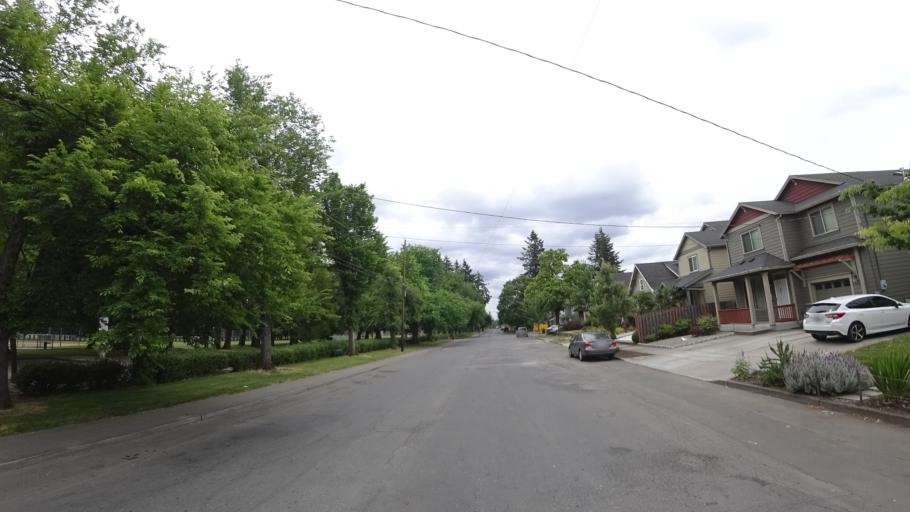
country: US
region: Oregon
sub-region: Multnomah County
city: Lents
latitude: 45.4898
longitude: -122.5723
